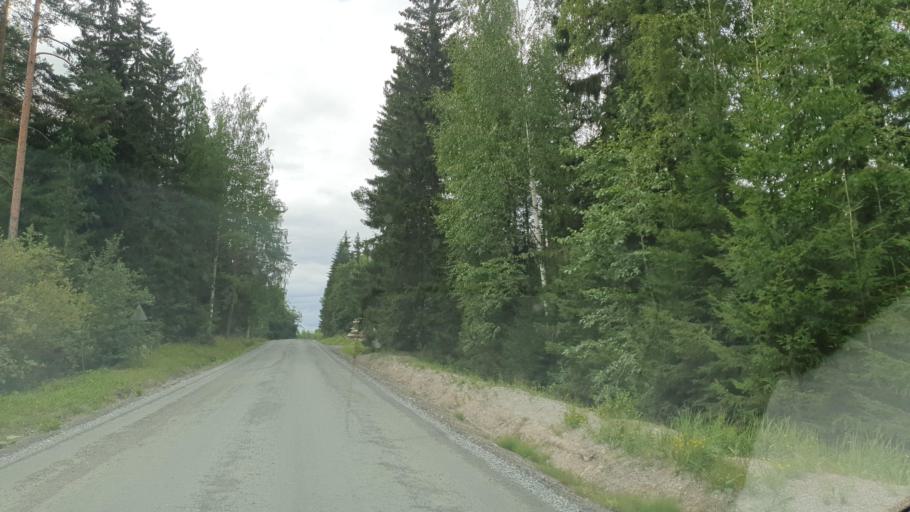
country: FI
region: Northern Savo
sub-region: Ylae-Savo
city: Iisalmi
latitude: 63.5149
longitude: 27.1150
